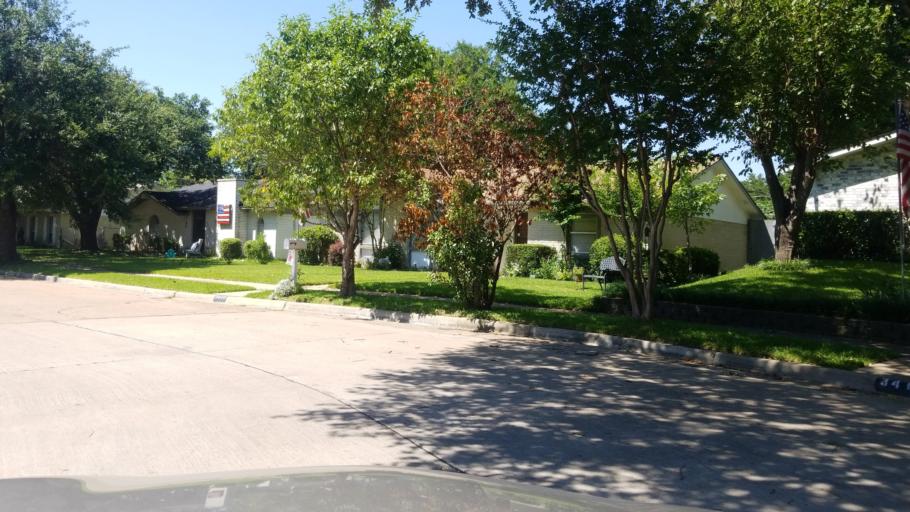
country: US
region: Texas
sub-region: Dallas County
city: Grand Prairie
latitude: 32.6910
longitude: -96.9948
